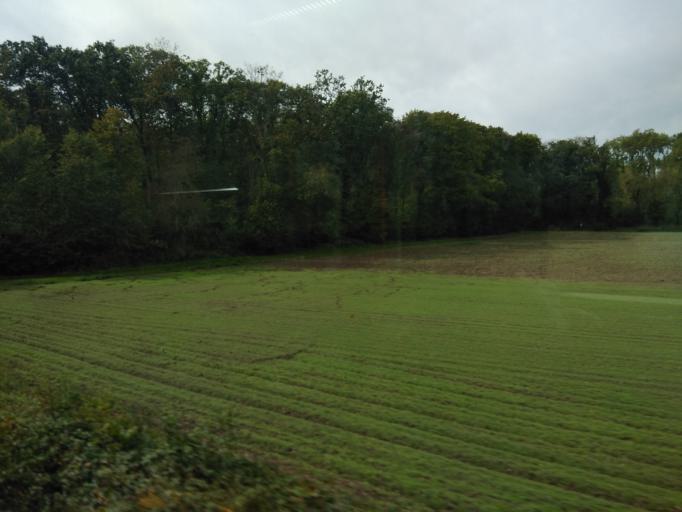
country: DE
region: Baden-Wuerttemberg
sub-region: Karlsruhe Region
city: Weingarten
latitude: 49.0782
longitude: 8.5392
